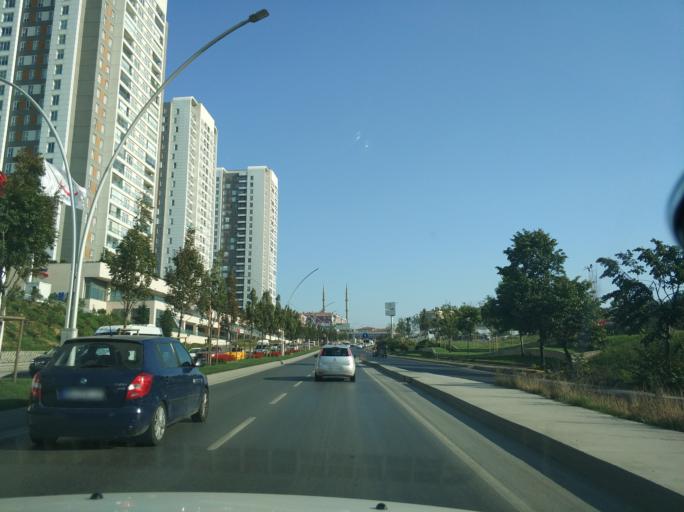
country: TR
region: Istanbul
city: Sultangazi
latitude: 41.0889
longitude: 28.9072
